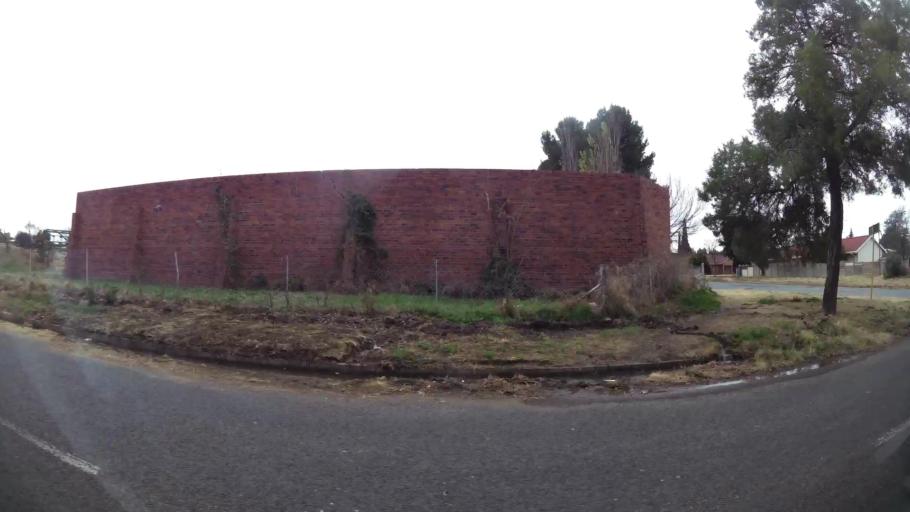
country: ZA
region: Orange Free State
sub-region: Fezile Dabi District Municipality
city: Kroonstad
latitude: -27.6364
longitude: 27.2383
